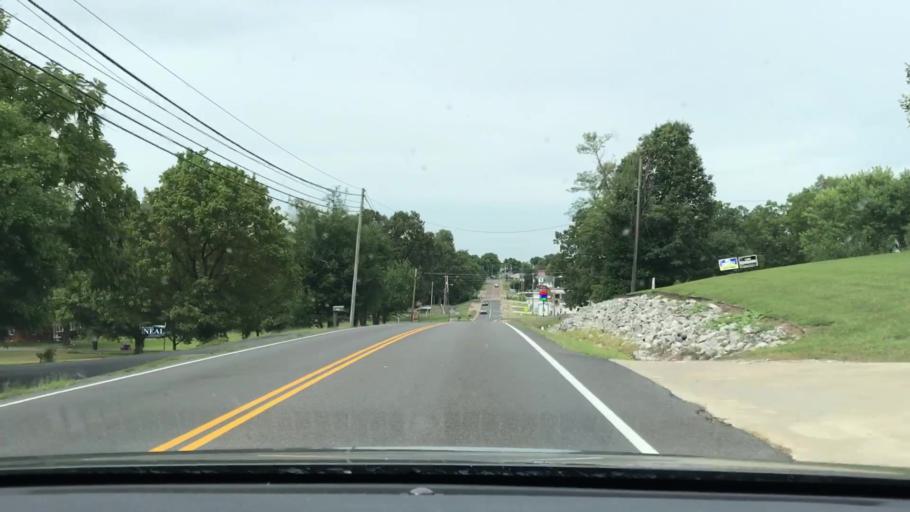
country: US
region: Kentucky
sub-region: Marshall County
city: Benton
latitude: 36.8490
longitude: -88.3502
